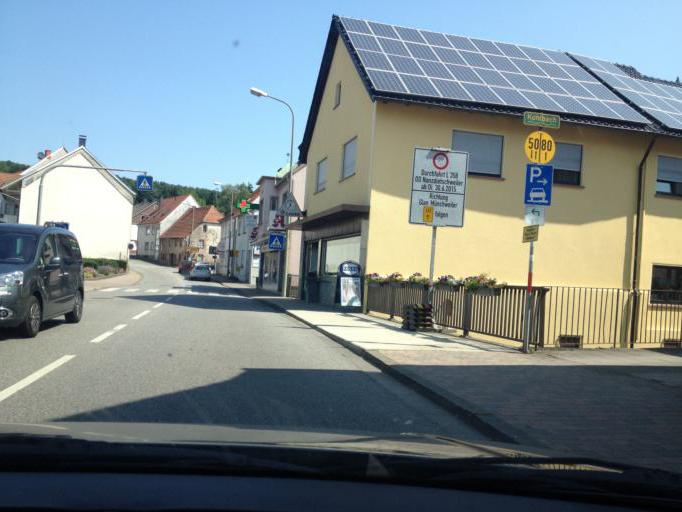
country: DE
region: Rheinland-Pfalz
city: Schonenberg-Kubelberg
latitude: 49.4100
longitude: 7.3765
